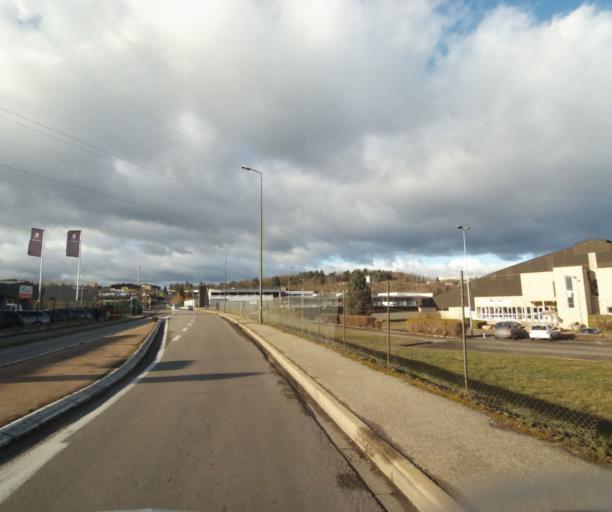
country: FR
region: Rhone-Alpes
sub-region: Departement de la Loire
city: La Talaudiere
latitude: 45.4753
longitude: 4.4268
